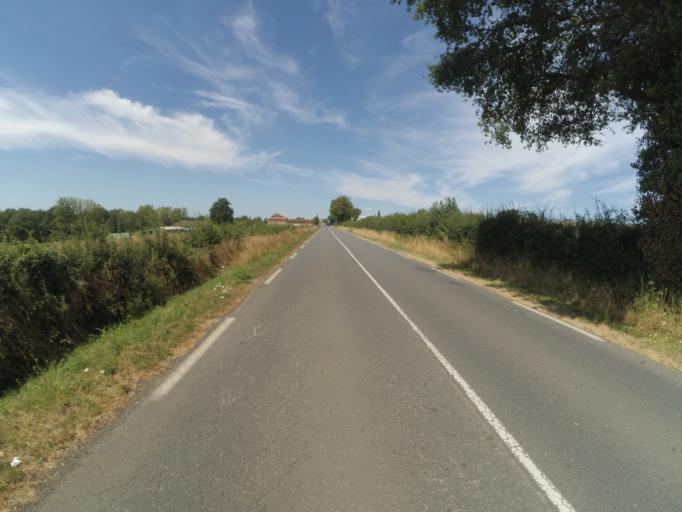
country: FR
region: Poitou-Charentes
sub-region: Departement de la Vienne
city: Availles-Limouzine
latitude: 46.1097
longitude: 0.5768
